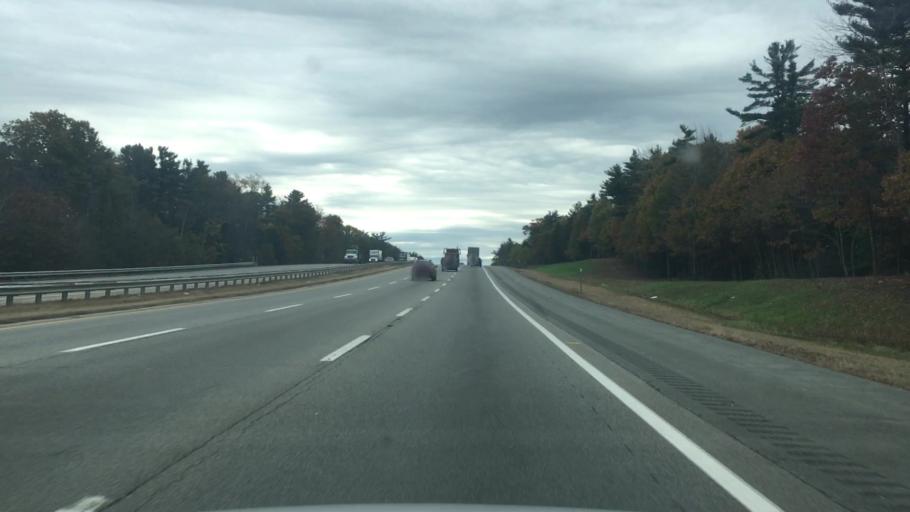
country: US
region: Maine
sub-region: Cumberland County
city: West Scarborough
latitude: 43.5724
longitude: -70.4056
